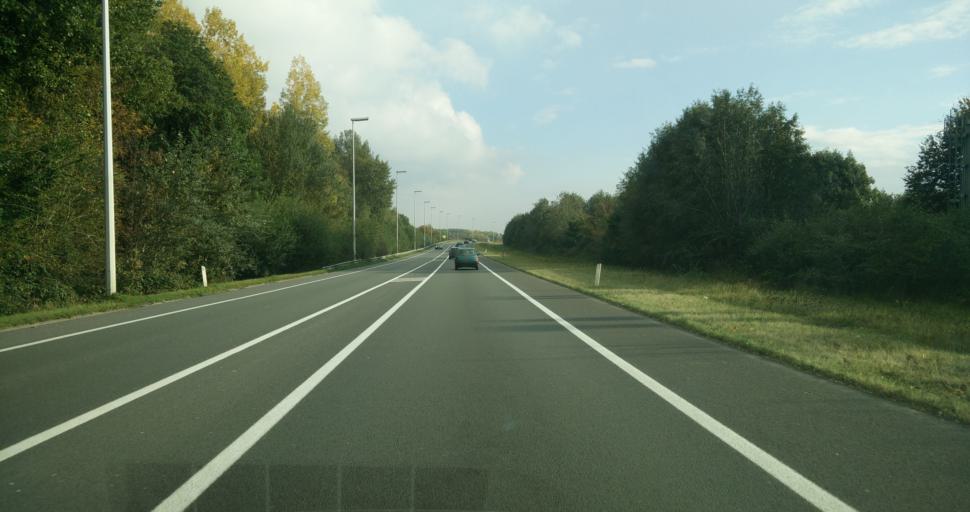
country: BE
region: Flanders
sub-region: Provincie Oost-Vlaanderen
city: Oosterzele
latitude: 50.9501
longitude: 3.8180
